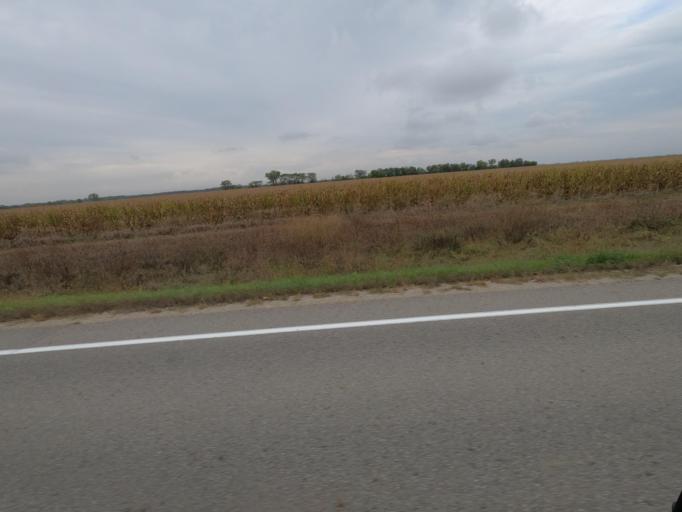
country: US
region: Iowa
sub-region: Van Buren County
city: Keosauqua
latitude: 40.8135
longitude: -91.8601
